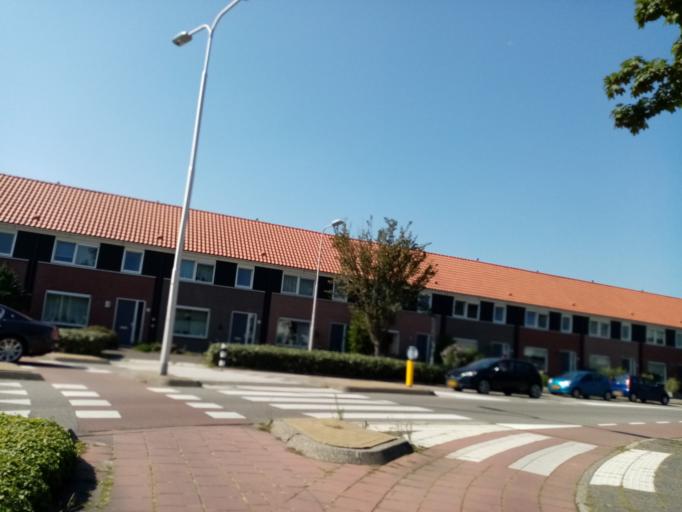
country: NL
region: South Holland
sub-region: Gemeente Lisse
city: Lisse
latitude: 52.2497
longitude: 4.5600
